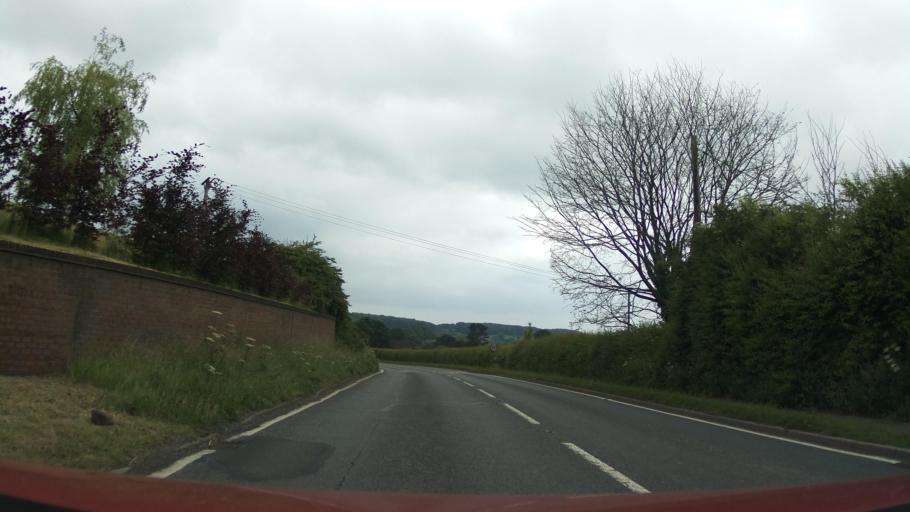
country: GB
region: England
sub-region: Derbyshire
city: Ashbourne
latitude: 53.0066
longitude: -1.7478
